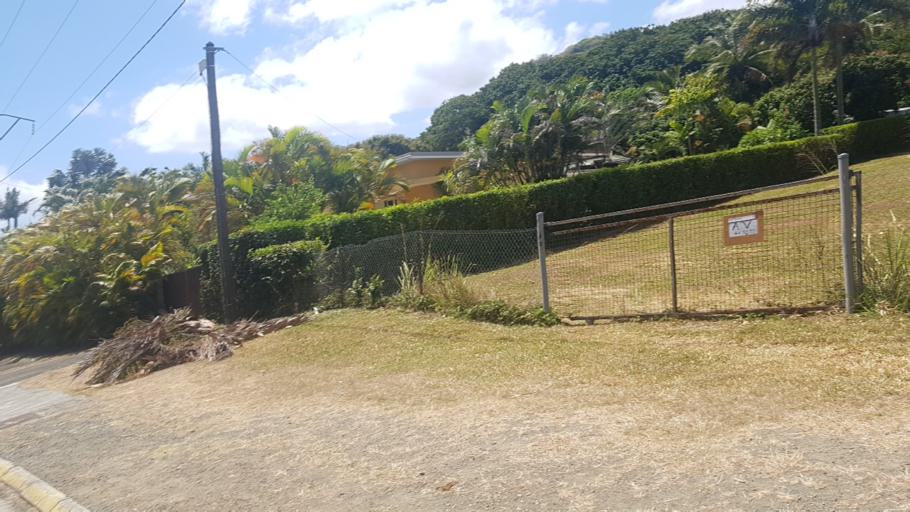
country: NC
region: South Province
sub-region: Dumbea
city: Dumbea
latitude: -22.1372
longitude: 166.4344
